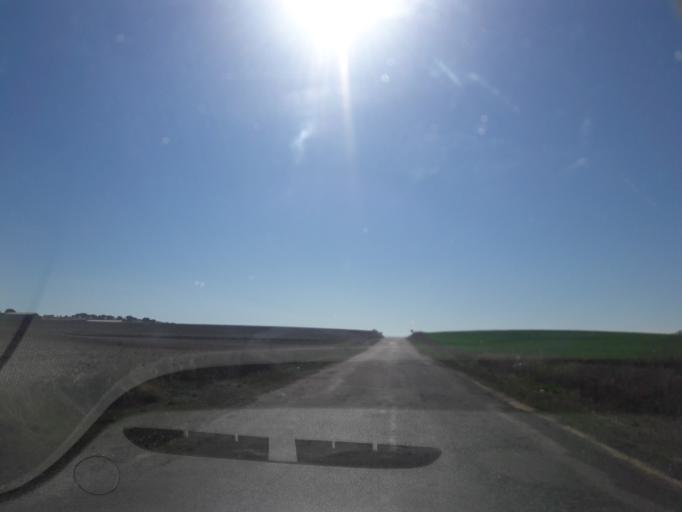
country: ES
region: Castille and Leon
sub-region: Provincia de Salamanca
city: Mancera de Abajo
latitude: 40.8250
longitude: -5.1796
